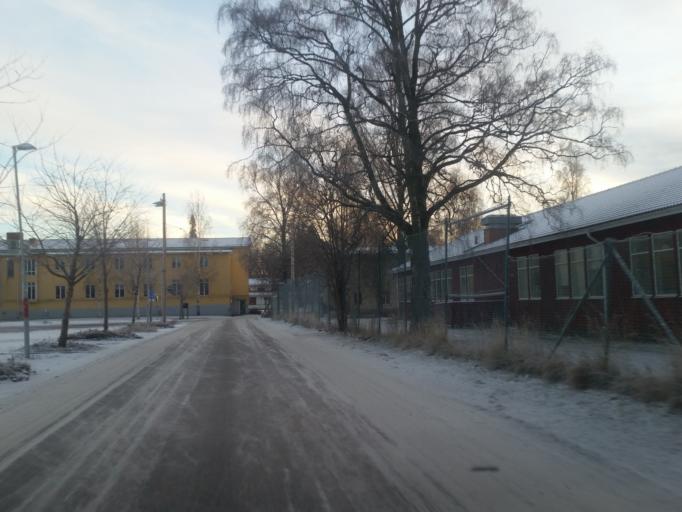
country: SE
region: Dalarna
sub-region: Leksand Municipality
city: Leksand
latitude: 60.7338
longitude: 14.9866
